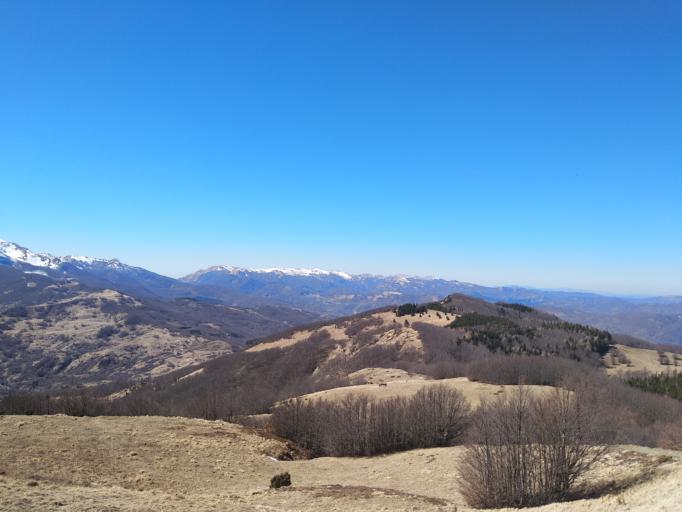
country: IT
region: Emilia-Romagna
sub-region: Provincia di Reggio Emilia
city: Collagna
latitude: 44.3767
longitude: 10.2839
